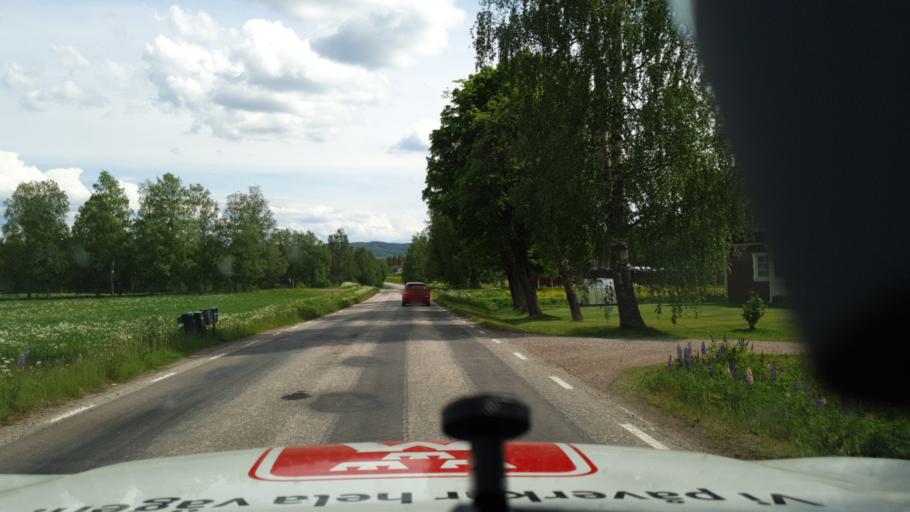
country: SE
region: Vaermland
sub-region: Torsby Kommun
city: Torsby
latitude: 59.9854
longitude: 12.8667
